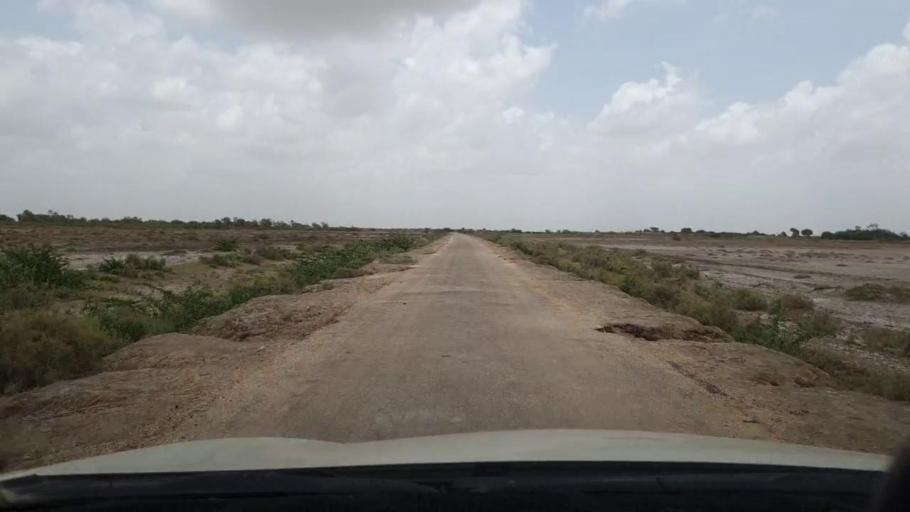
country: PK
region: Sindh
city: Kadhan
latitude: 24.3602
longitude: 68.9302
